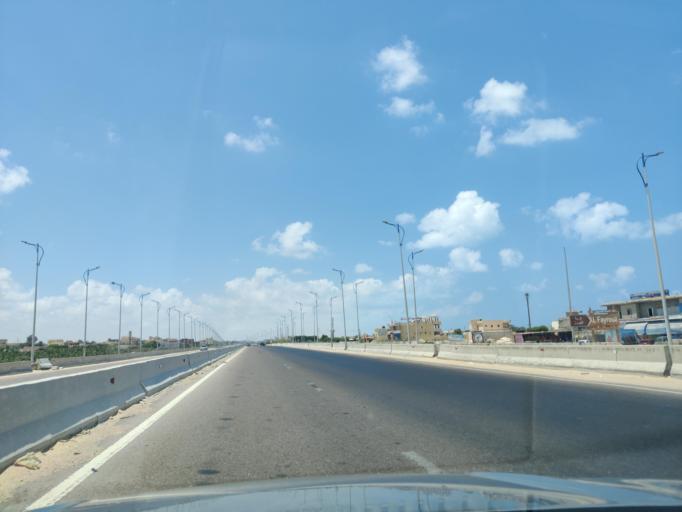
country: EG
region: Alexandria
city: Alexandria
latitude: 30.9816
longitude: 29.5795
